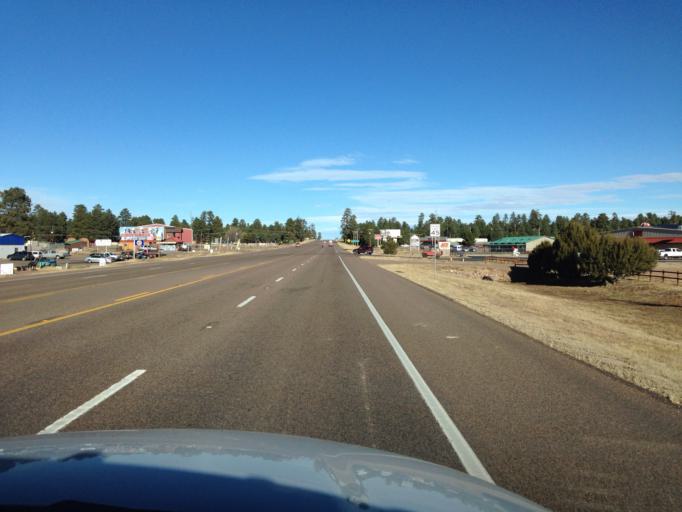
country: US
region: Arizona
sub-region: Navajo County
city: Heber-Overgaard
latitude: 34.4037
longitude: -110.5644
